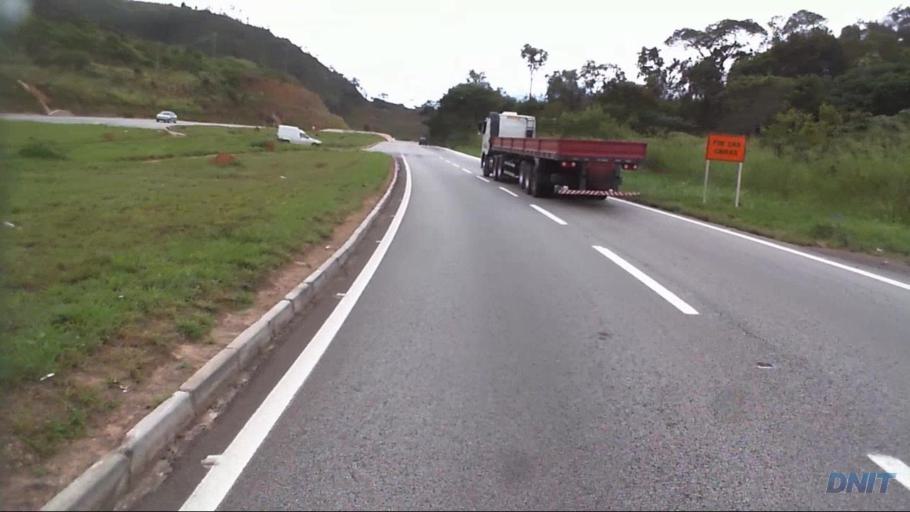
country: BR
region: Minas Gerais
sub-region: Caete
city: Caete
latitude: -19.7925
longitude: -43.6801
